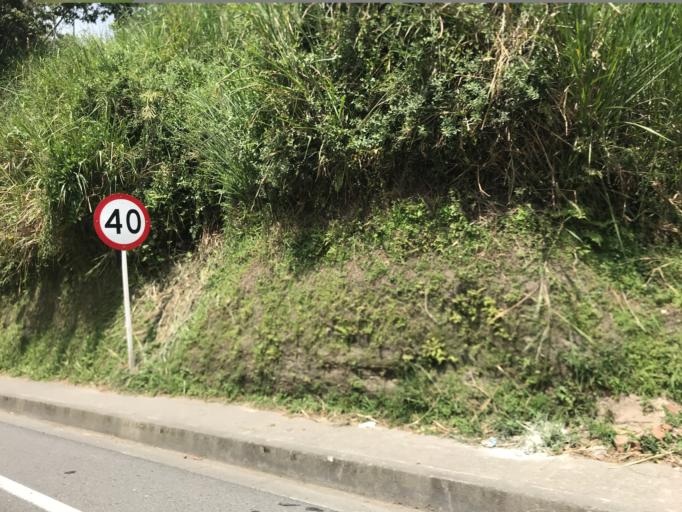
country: CO
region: Quindio
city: Calarca
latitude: 4.5190
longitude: -75.6470
